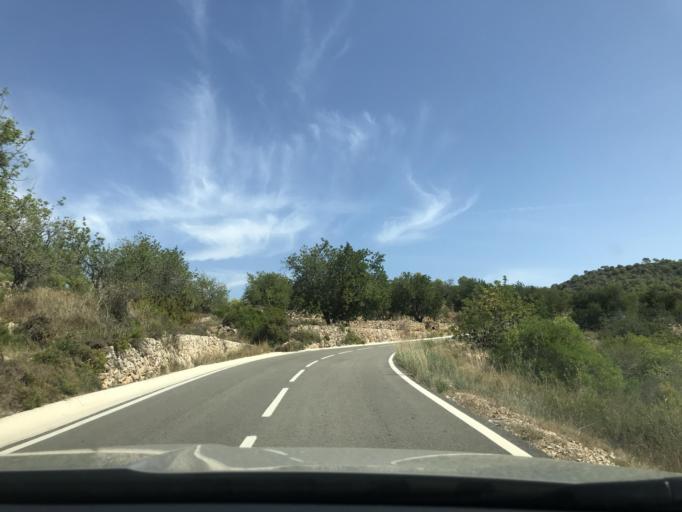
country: ES
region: Catalonia
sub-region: Provincia de Tarragona
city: Salomo
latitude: 41.2027
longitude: 1.3867
